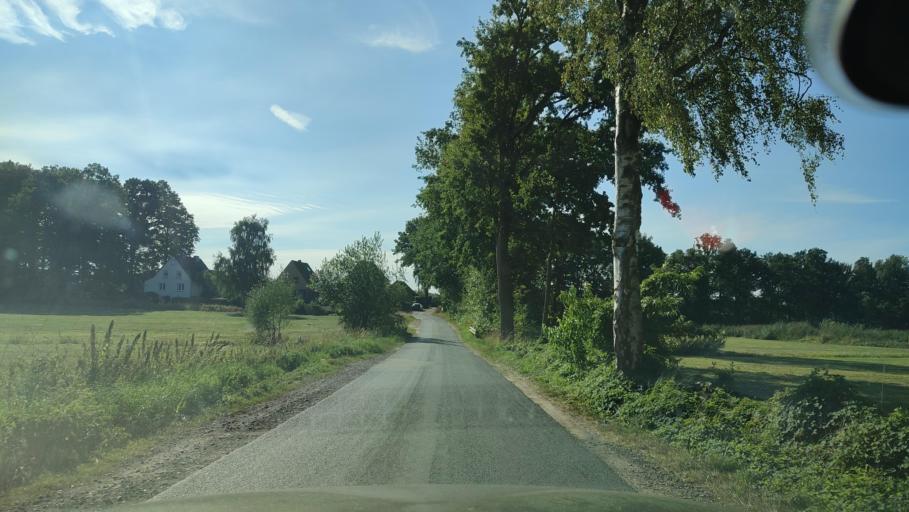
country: DE
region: Lower Saxony
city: Bomlitz
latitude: 52.8888
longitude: 9.6727
